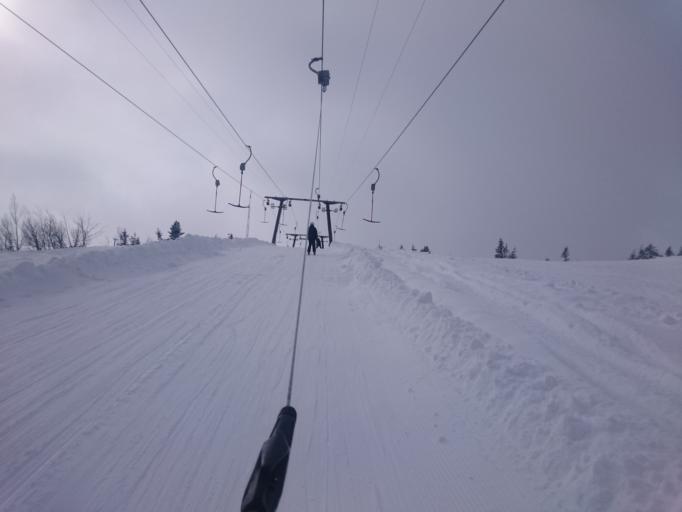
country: SE
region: Dalarna
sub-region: Malung-Saelens kommun
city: Malung
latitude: 61.1616
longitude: 13.1664
